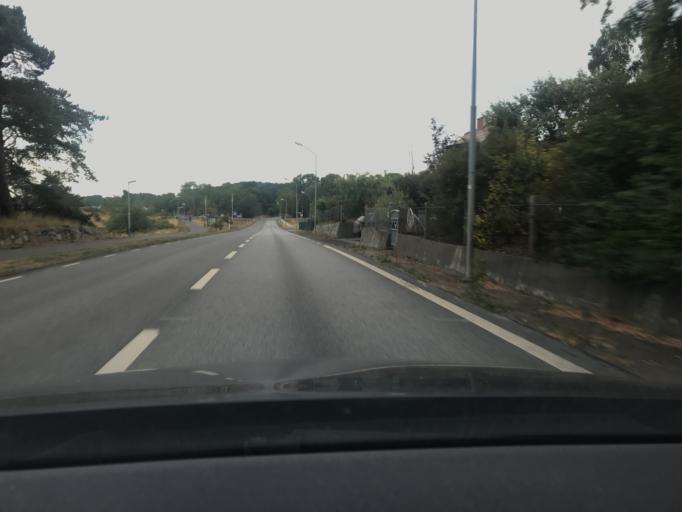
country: SE
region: Skane
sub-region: Simrishamns Kommun
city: Simrishamn
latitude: 55.5742
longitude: 14.3345
